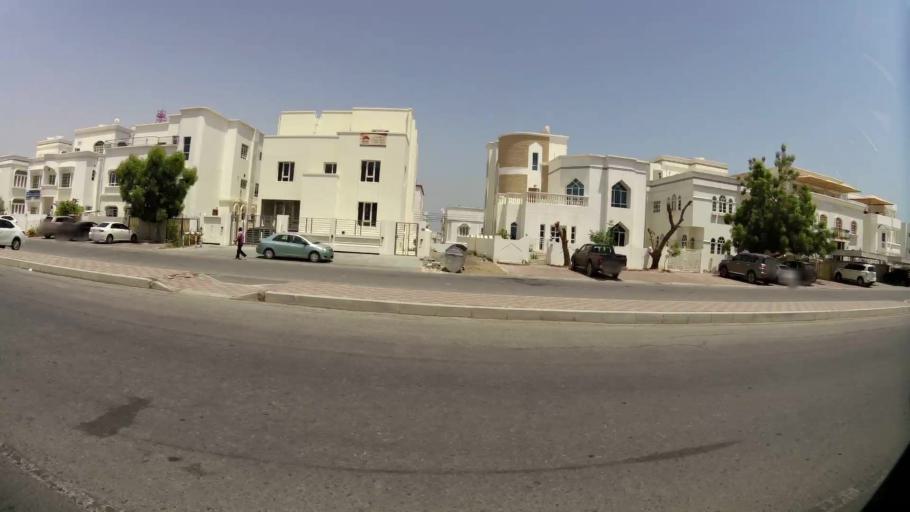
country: OM
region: Muhafazat Masqat
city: Bawshar
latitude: 23.5843
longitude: 58.4385
